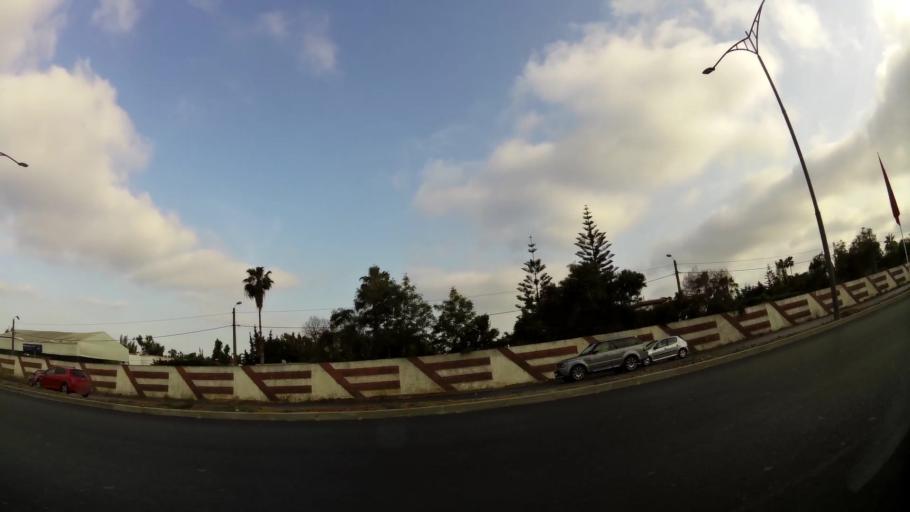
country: MA
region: Rabat-Sale-Zemmour-Zaer
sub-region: Rabat
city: Rabat
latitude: 33.9579
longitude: -6.8305
